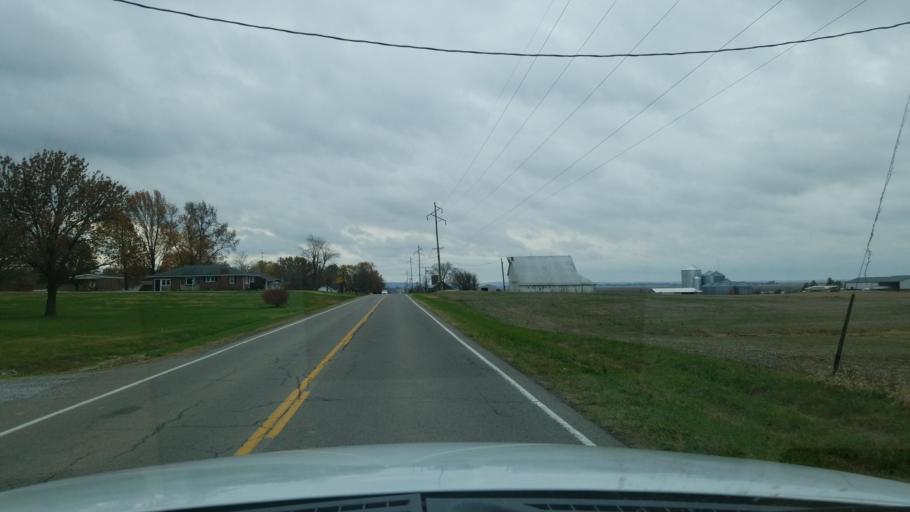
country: US
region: Illinois
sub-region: Saline County
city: Eldorado
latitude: 37.7958
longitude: -88.4383
